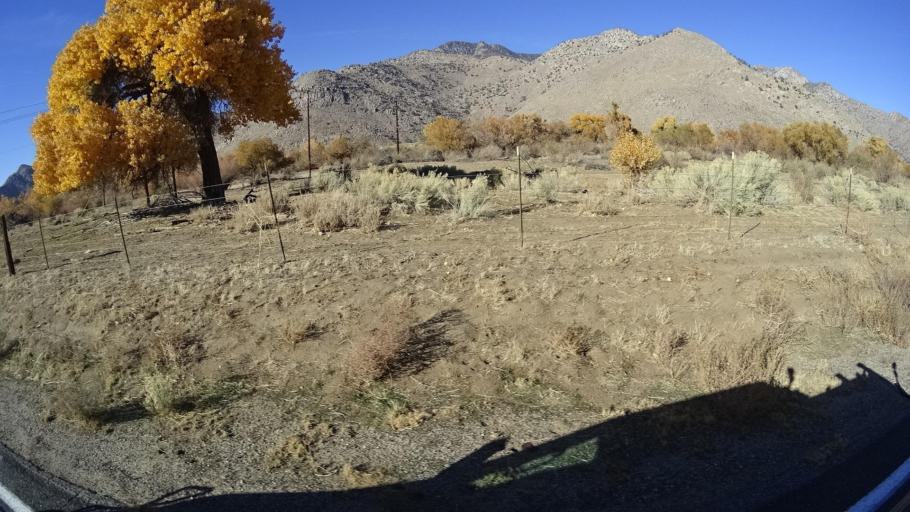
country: US
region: California
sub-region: Kern County
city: Weldon
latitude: 35.6855
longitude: -118.2417
